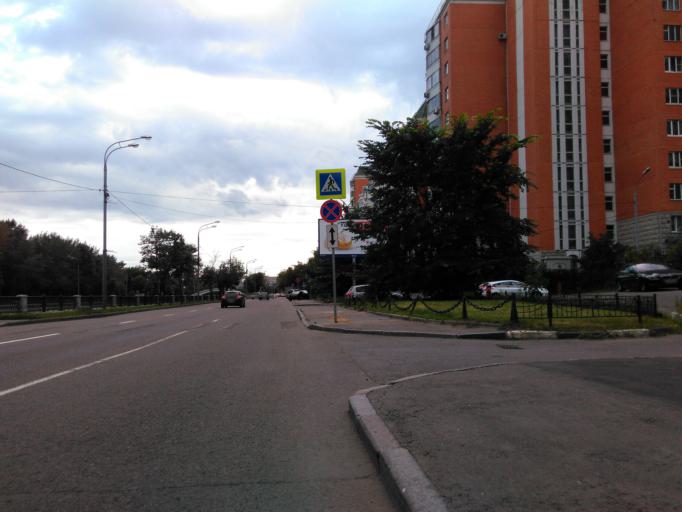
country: RU
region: Moscow
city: Lefortovo
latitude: 55.7763
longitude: 37.7002
